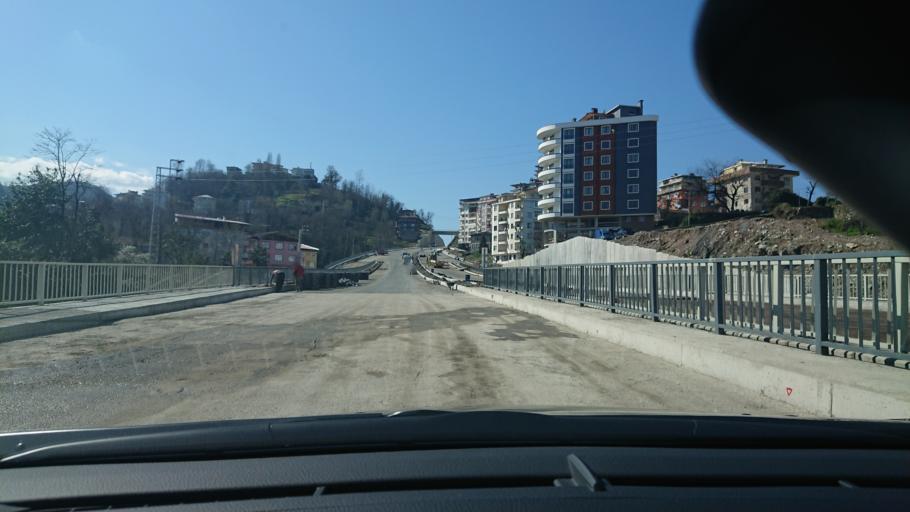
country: TR
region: Rize
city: Rize
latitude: 41.0209
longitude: 40.5248
